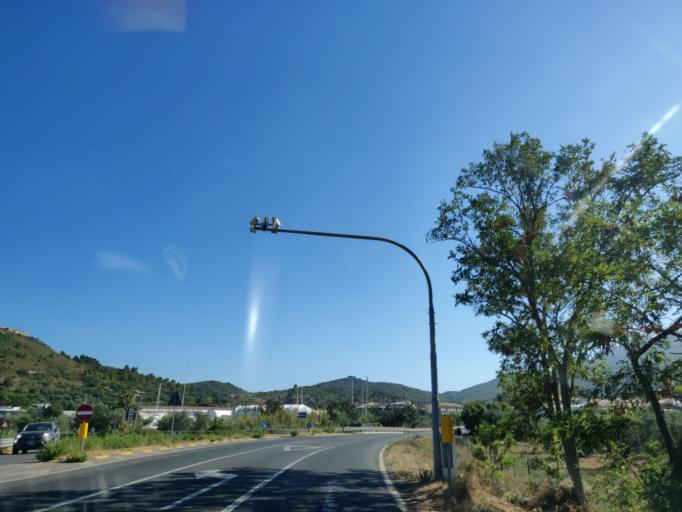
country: IT
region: Tuscany
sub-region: Provincia di Grosseto
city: Porto Ercole
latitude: 42.4046
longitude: 11.2004
